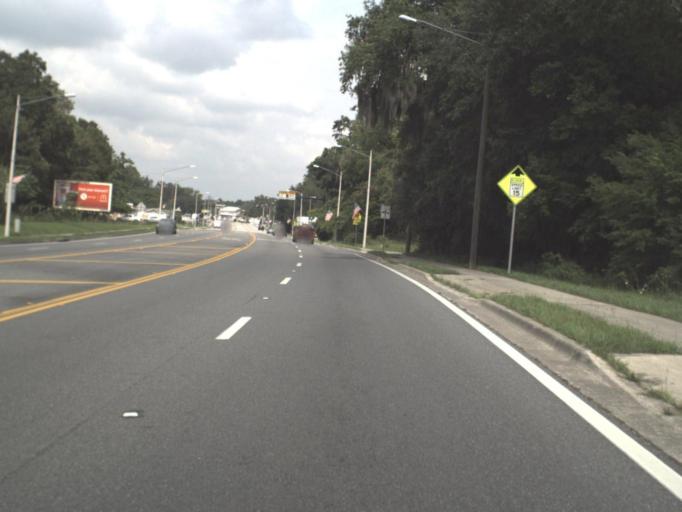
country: US
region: Florida
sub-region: Levy County
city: Williston
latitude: 29.3887
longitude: -82.4328
